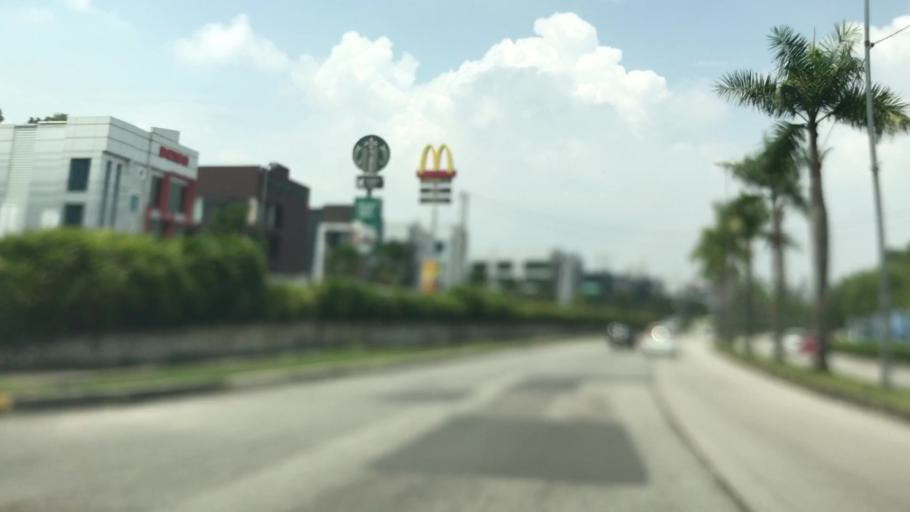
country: MY
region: Selangor
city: Subang Jaya
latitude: 3.0210
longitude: 101.6243
